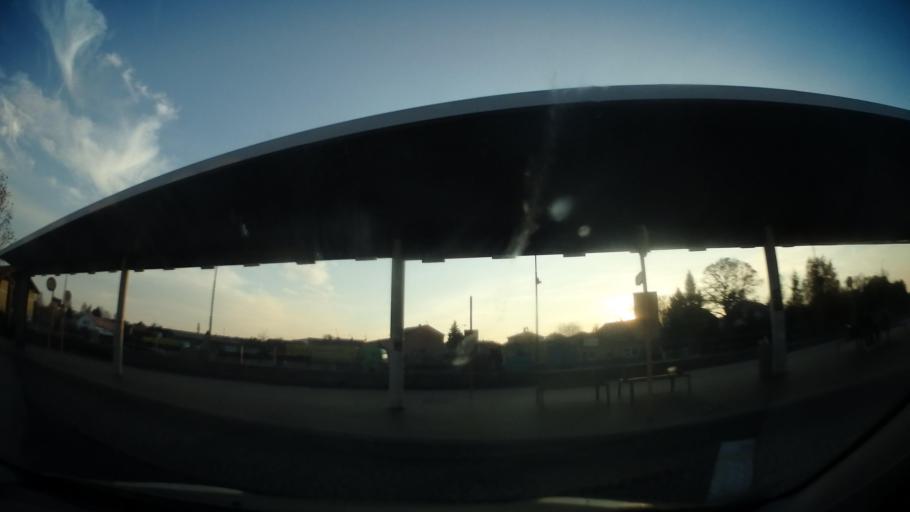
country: CZ
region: Central Bohemia
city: Vlasim
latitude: 49.7002
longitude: 14.8986
